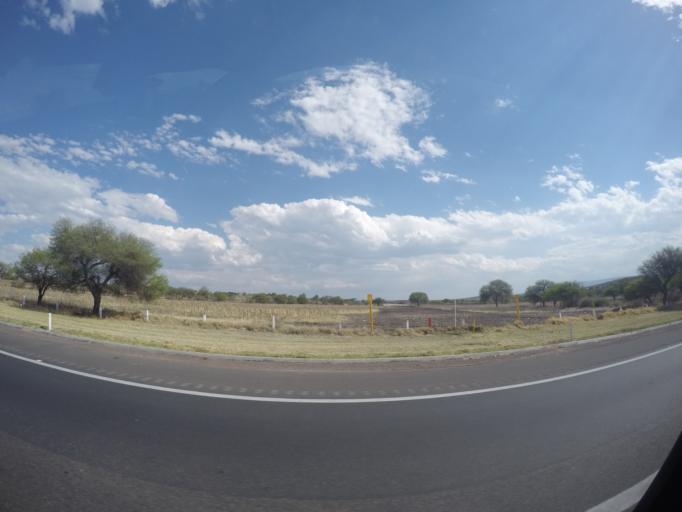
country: MX
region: Guanajuato
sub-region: Apaseo el Grande
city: Coachiti
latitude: 20.5380
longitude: -100.6048
